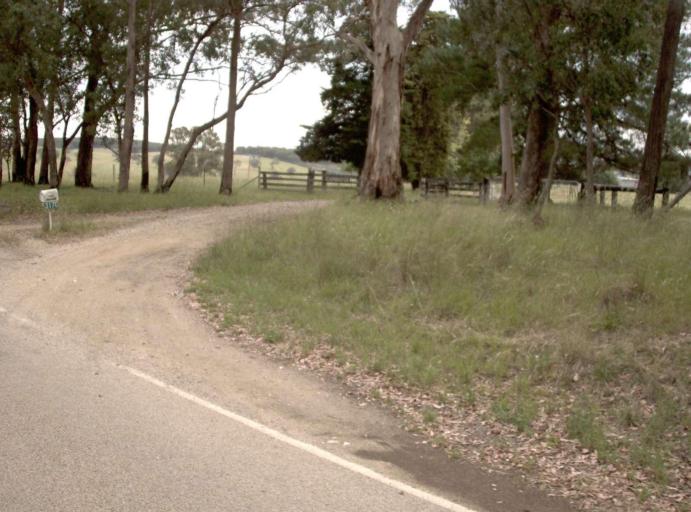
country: AU
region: Victoria
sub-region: East Gippsland
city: Bairnsdale
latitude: -37.7411
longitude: 147.3133
